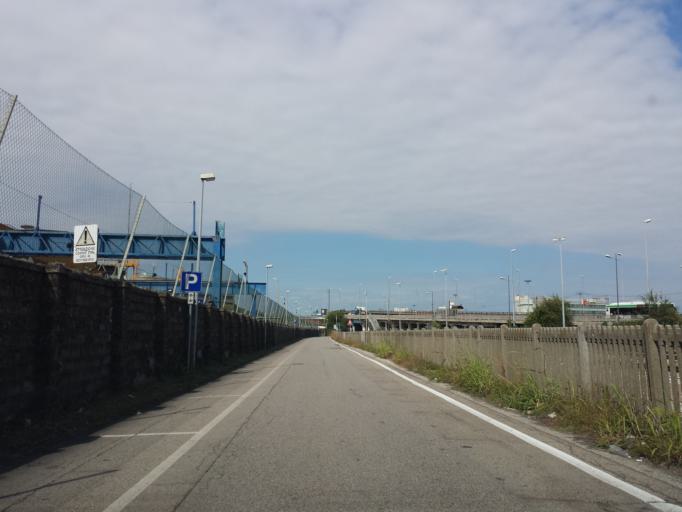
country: IT
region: Veneto
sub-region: Provincia di Venezia
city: Mestre
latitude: 45.4779
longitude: 12.2441
